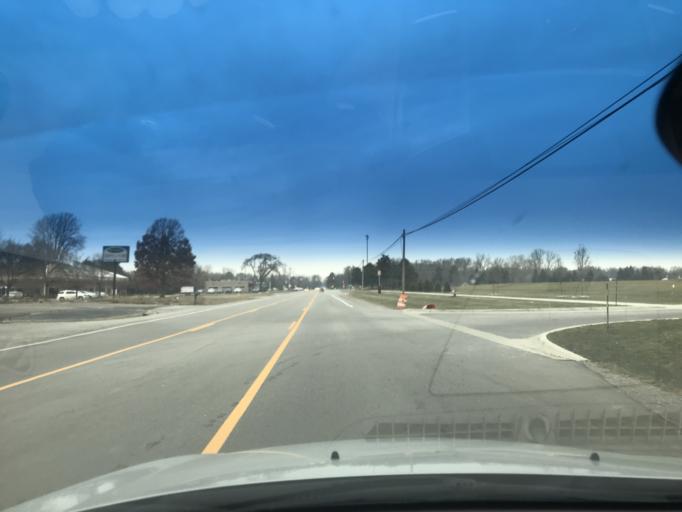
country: US
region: Michigan
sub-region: Macomb County
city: Shelby
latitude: 42.6662
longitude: -83.0534
